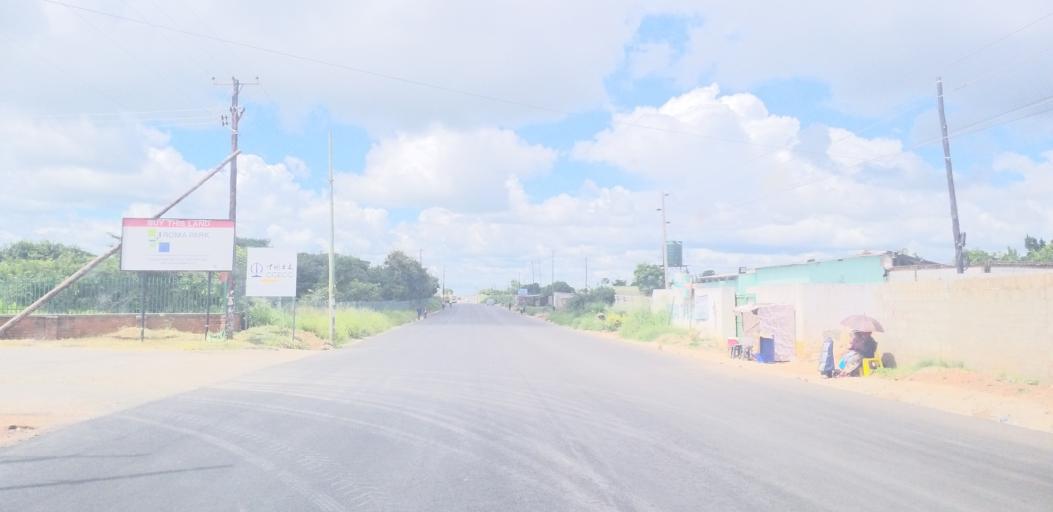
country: ZM
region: Lusaka
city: Lusaka
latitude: -15.3571
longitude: 28.3231
